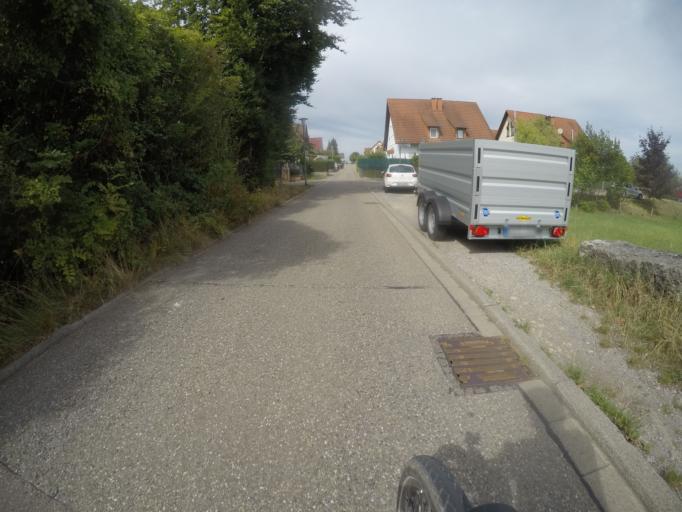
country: DE
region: Baden-Wuerttemberg
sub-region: Karlsruhe Region
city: Eutingen
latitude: 48.8822
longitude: 8.7624
